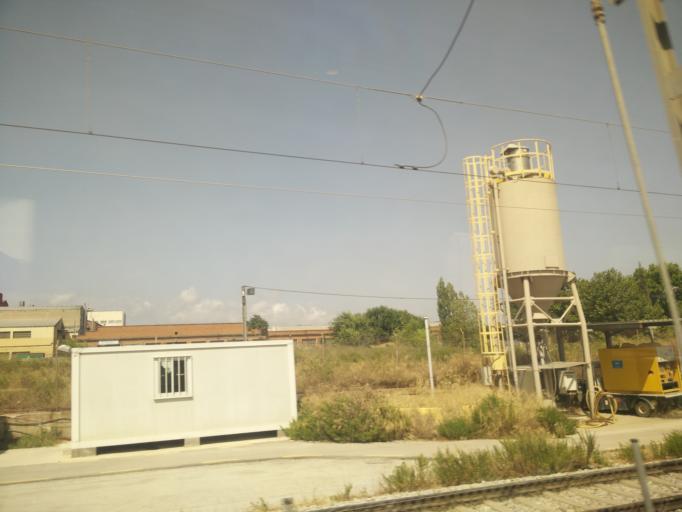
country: ES
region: Catalonia
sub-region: Provincia de Barcelona
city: Sant Marti
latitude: 41.4298
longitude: 2.2027
